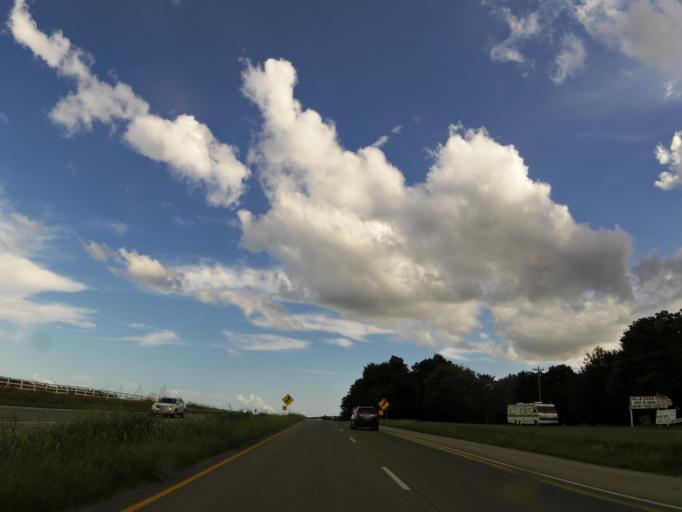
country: US
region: Kentucky
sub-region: Christian County
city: Hopkinsville
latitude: 36.7697
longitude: -87.4717
